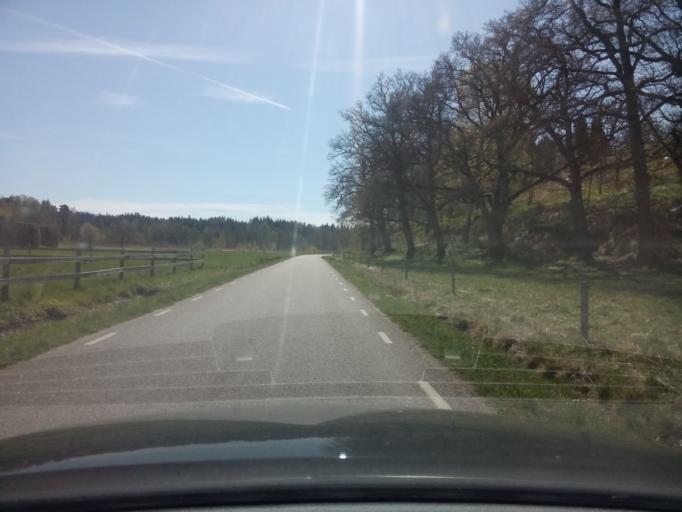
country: SE
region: Soedermanland
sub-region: Trosa Kommun
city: Trosa
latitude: 58.8080
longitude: 17.3623
